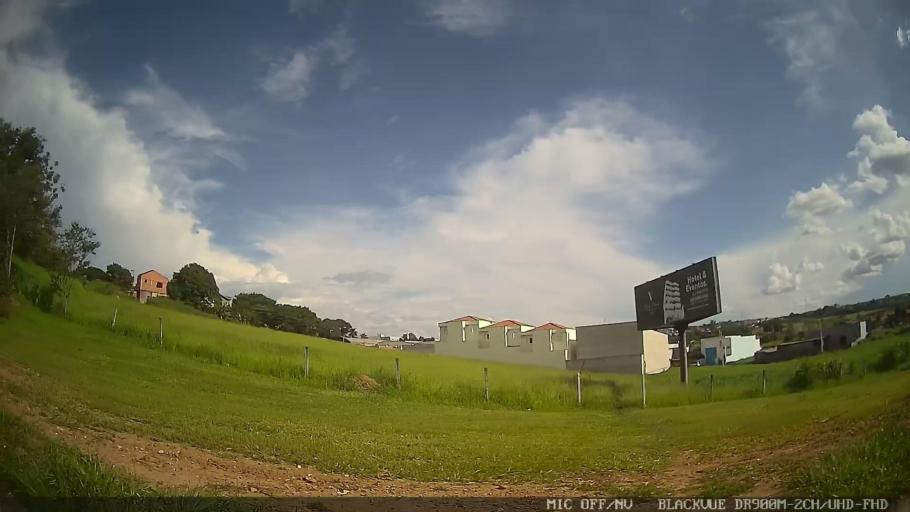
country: BR
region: Sao Paulo
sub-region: Laranjal Paulista
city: Laranjal Paulista
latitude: -23.0404
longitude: -47.8392
